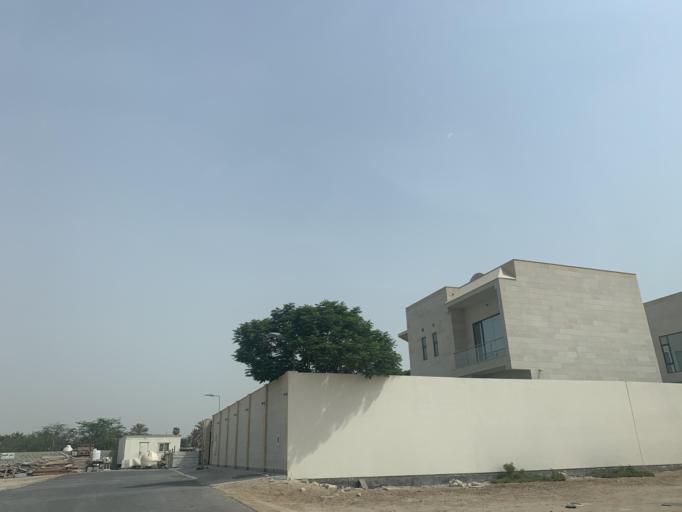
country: BH
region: Manama
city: Jidd Hafs
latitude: 26.1982
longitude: 50.4702
